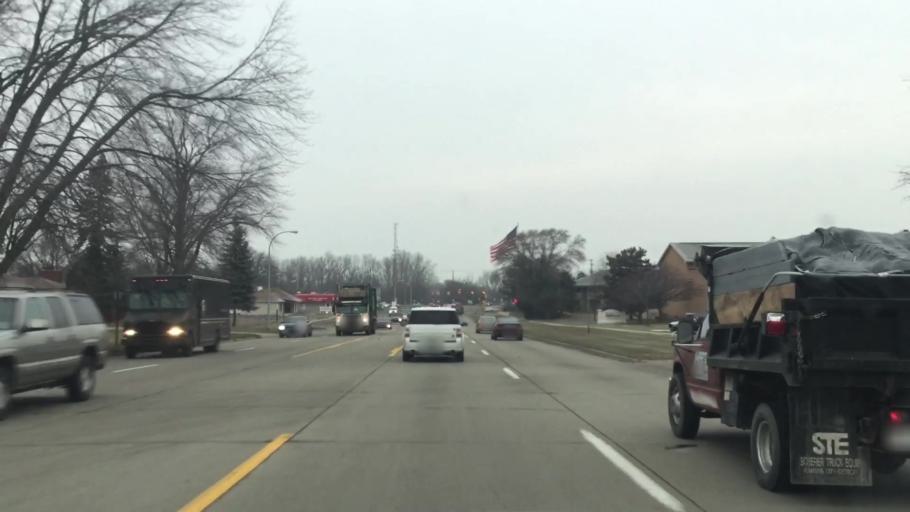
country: US
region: Michigan
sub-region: Wayne County
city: Garden City
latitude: 42.3359
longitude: -83.3508
